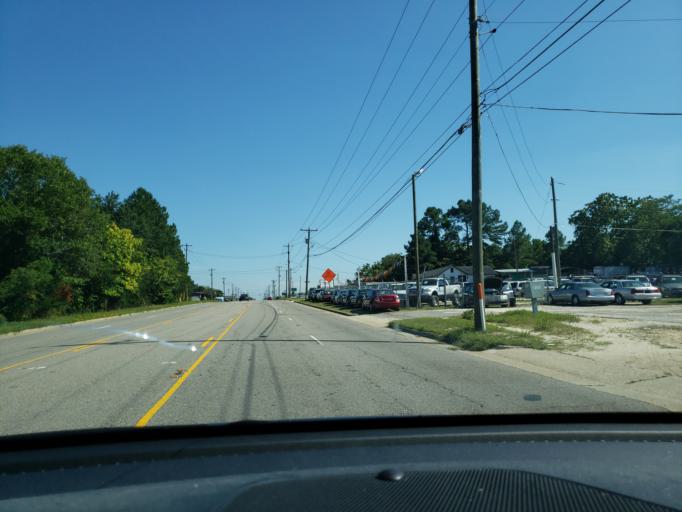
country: US
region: North Carolina
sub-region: Cumberland County
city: Spring Lake
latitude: 35.1171
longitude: -78.9325
